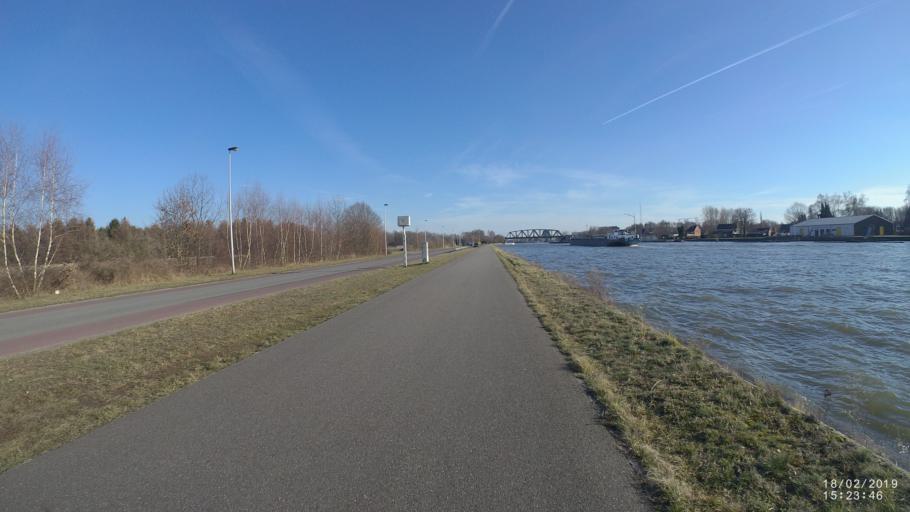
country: BE
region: Flanders
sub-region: Provincie Limburg
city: Hasselt
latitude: 50.9515
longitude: 5.3211
